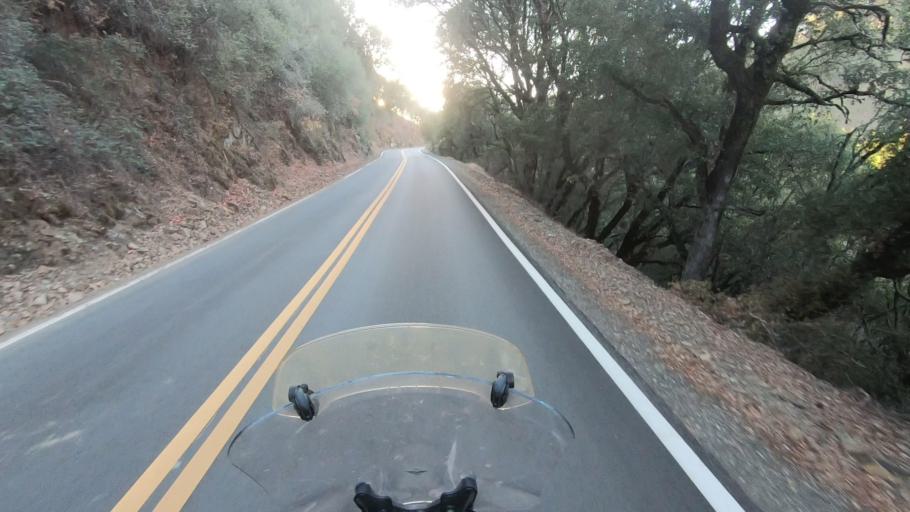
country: US
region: California
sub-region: Santa Clara County
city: East Foothills
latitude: 37.3283
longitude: -121.6769
